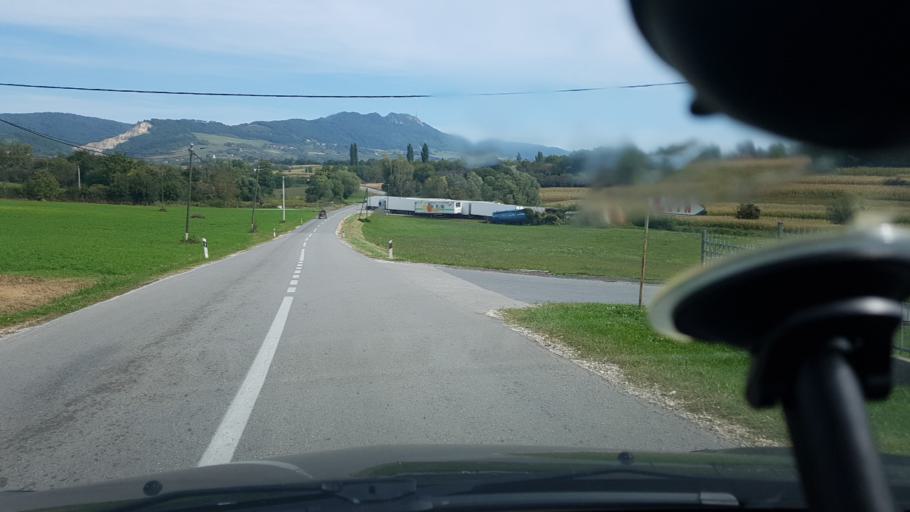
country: HR
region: Varazdinska
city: Ljubescica
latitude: 46.1035
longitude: 16.4133
